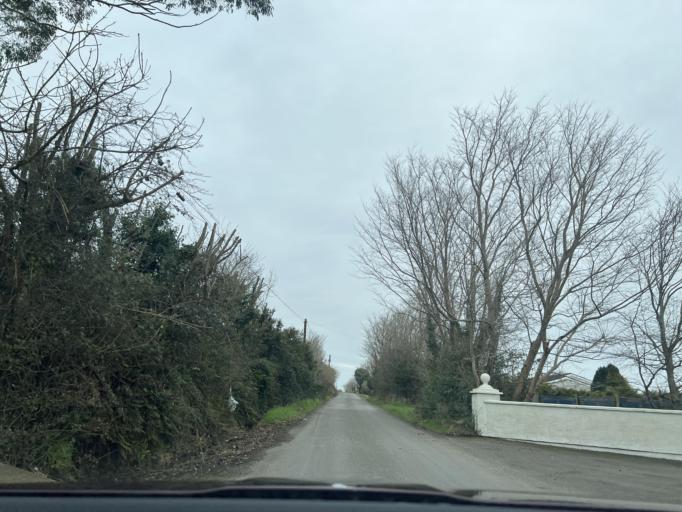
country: IE
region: Leinster
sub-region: Loch Garman
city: Castlebridge
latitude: 52.3731
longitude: -6.5228
